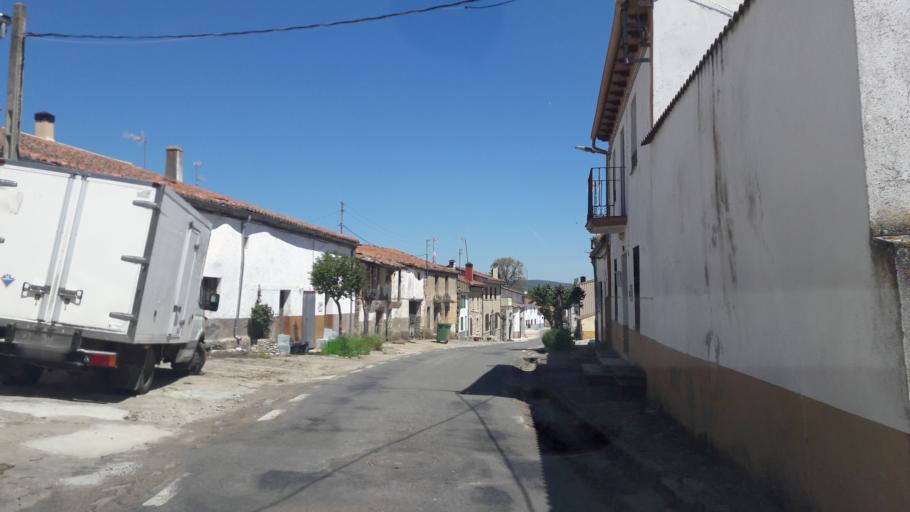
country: ES
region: Castille and Leon
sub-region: Provincia de Salamanca
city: Endrinal
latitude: 40.5904
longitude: -5.8038
